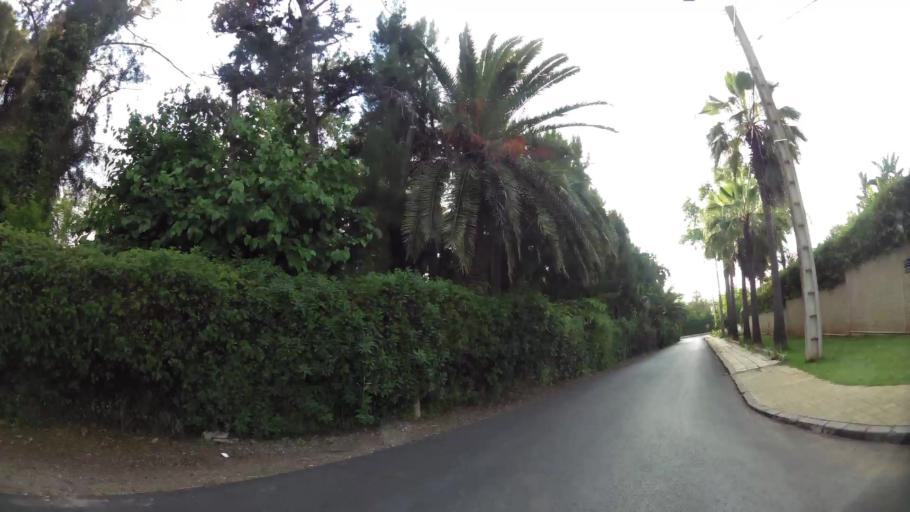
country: MA
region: Rabat-Sale-Zemmour-Zaer
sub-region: Rabat
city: Rabat
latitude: 33.9655
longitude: -6.8492
